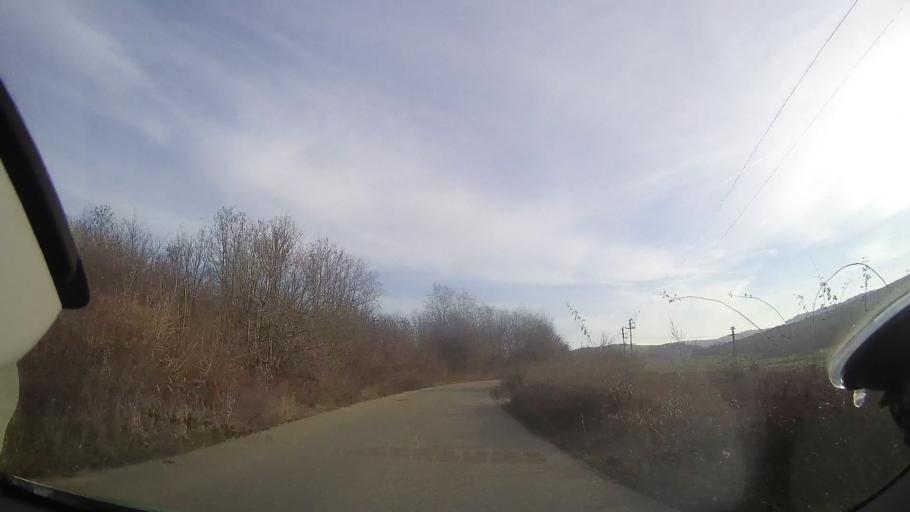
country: RO
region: Bihor
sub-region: Comuna Sarbi
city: Sarbi
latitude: 47.1852
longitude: 22.1298
